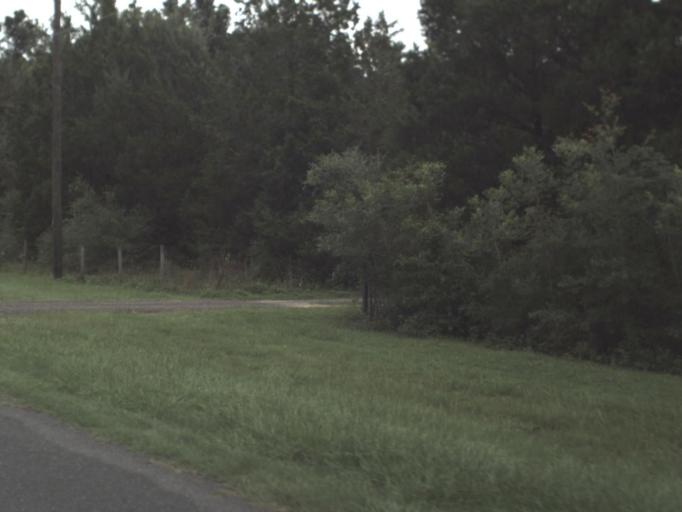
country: US
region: Florida
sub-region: Levy County
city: Williston
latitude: 29.2758
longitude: -82.4436
